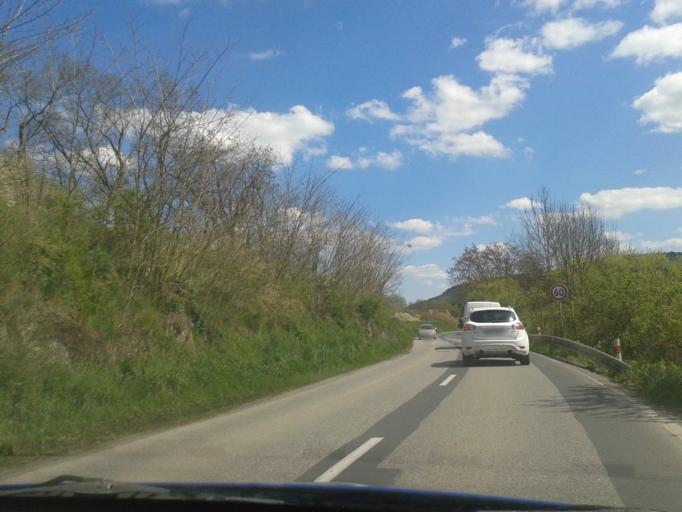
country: CZ
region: Central Bohemia
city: Hyskov
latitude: 49.9924
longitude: 14.0308
